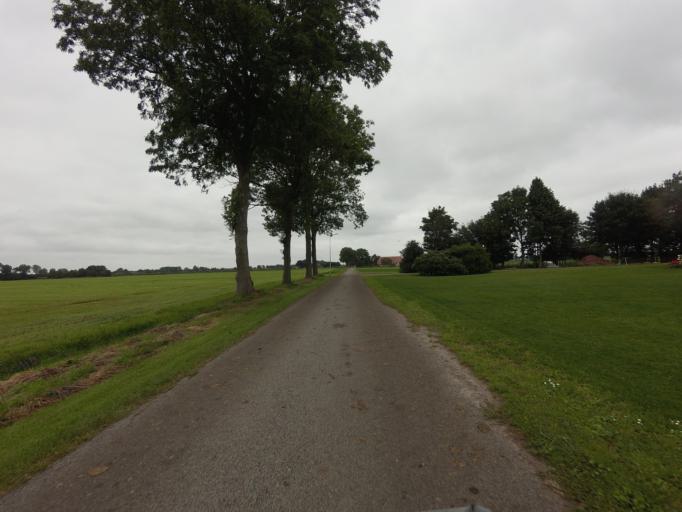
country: NL
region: Overijssel
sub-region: Gemeente Steenwijkerland
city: Blokzijl
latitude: 52.7375
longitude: 6.0085
